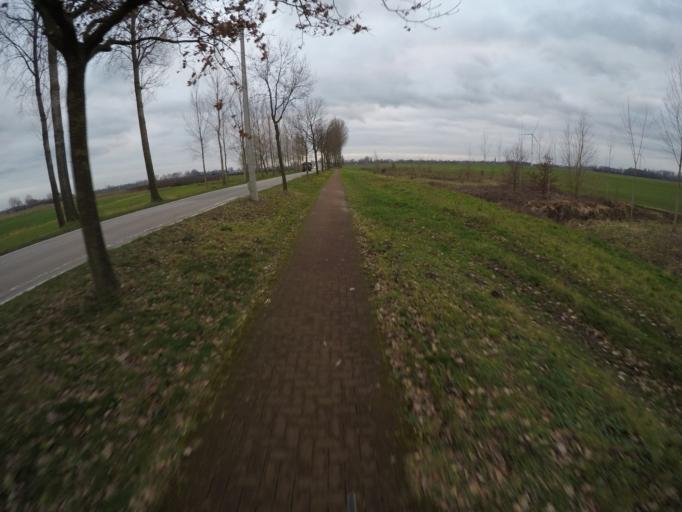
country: BE
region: Flanders
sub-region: Provincie Oost-Vlaanderen
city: Sint-Gillis-Waas
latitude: 51.2388
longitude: 4.1468
